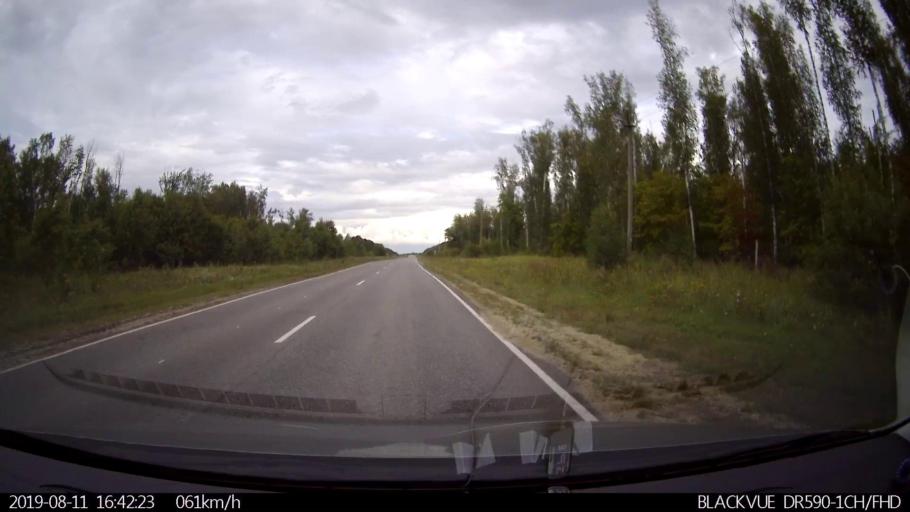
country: RU
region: Ulyanovsk
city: Mayna
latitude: 54.1601
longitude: 47.6618
